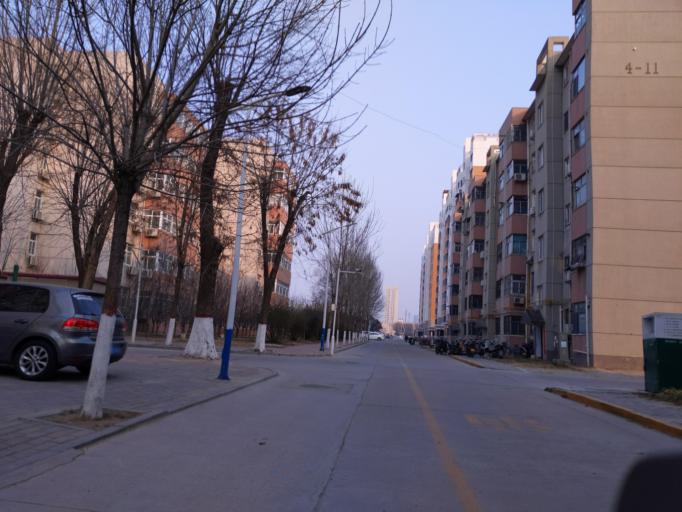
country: CN
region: Henan Sheng
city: Zhongyuanlu
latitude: 35.7799
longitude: 115.0532
